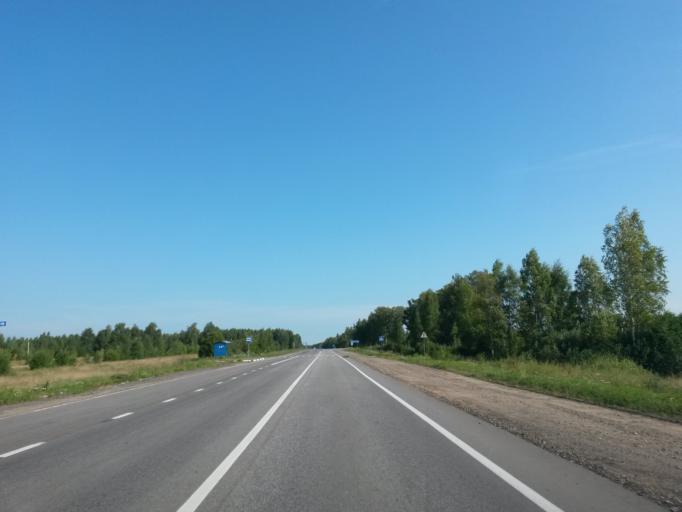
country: RU
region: Jaroslavl
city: Gavrilov-Yam
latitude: 57.3577
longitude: 39.9083
